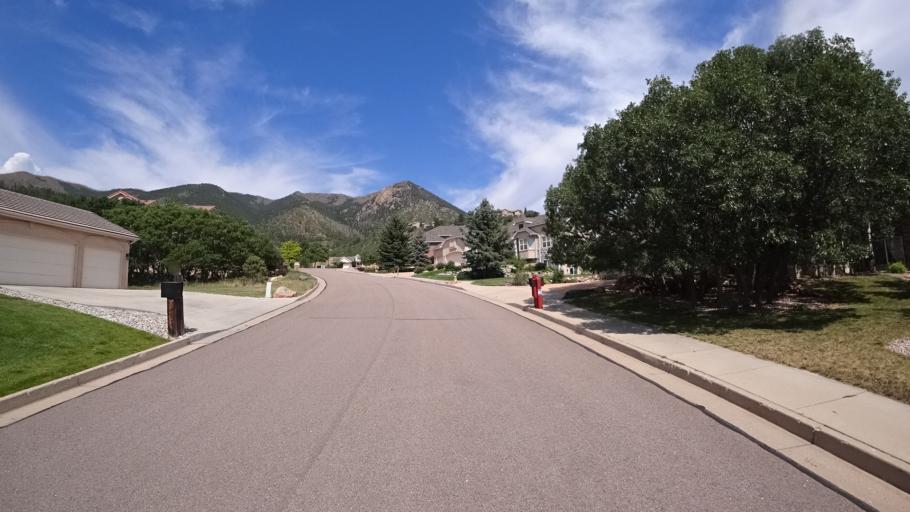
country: US
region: Colorado
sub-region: El Paso County
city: Air Force Academy
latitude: 38.9489
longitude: -104.8830
